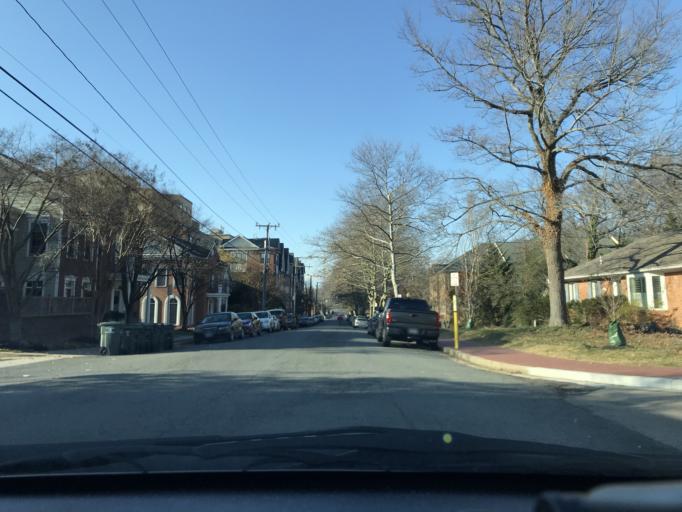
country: US
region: Virginia
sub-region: City of Falls Church
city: Falls Church
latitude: 38.8864
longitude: -77.1751
